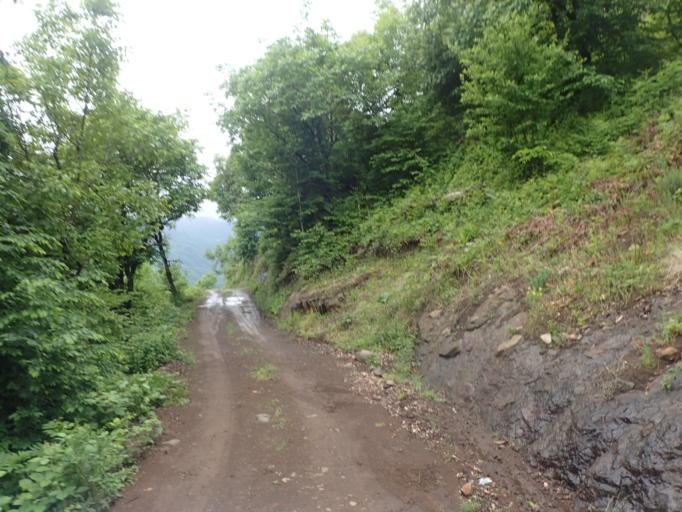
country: TR
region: Samsun
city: Salipazari
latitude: 40.9448
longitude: 36.8939
